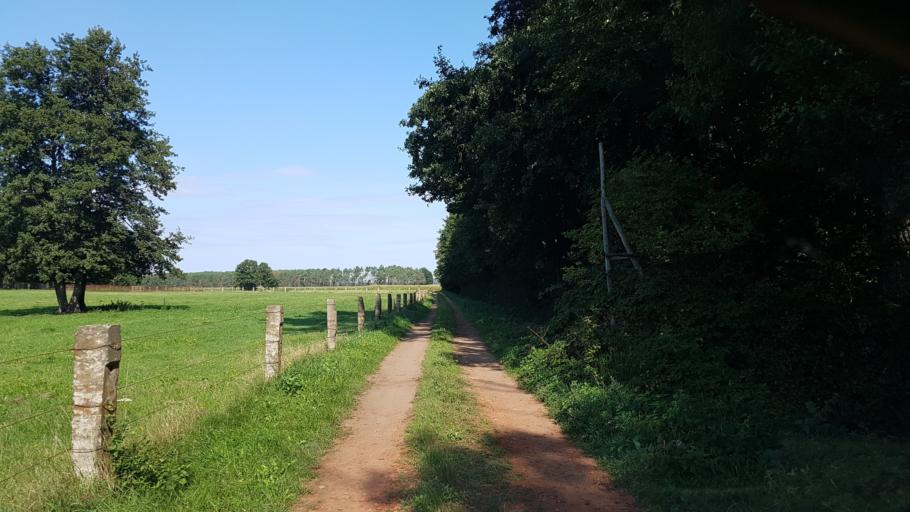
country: DE
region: Brandenburg
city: Schonewalde
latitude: 51.6648
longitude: 13.6204
